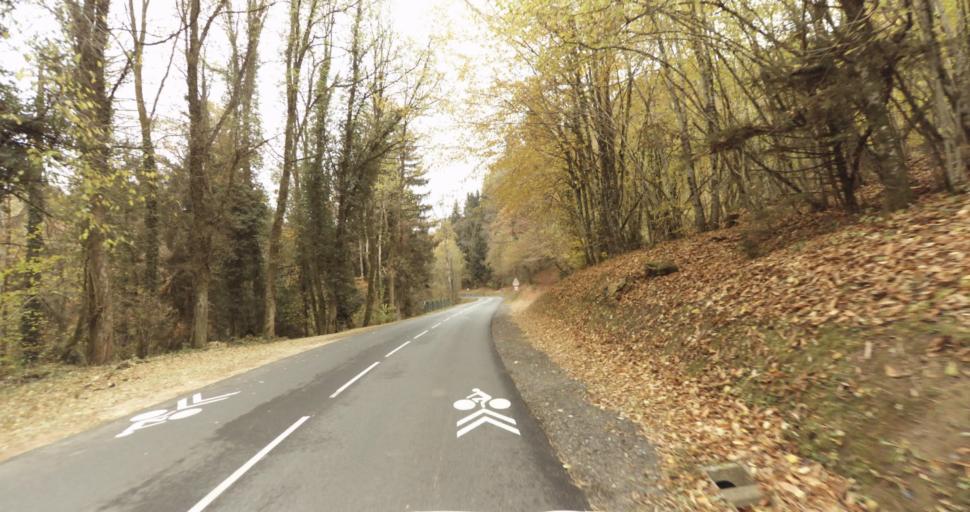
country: FR
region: Rhone-Alpes
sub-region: Departement de la Haute-Savoie
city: Sevrier
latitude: 45.8436
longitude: 6.1380
